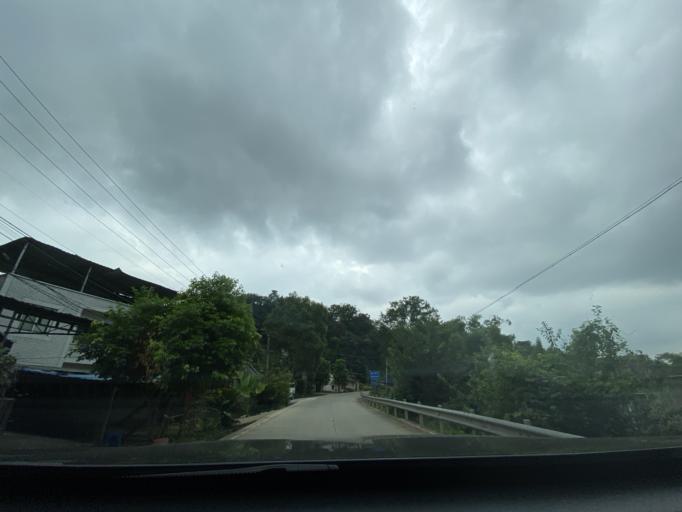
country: CN
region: Sichuan
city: Dongsheng
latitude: 30.4067
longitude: 104.0093
